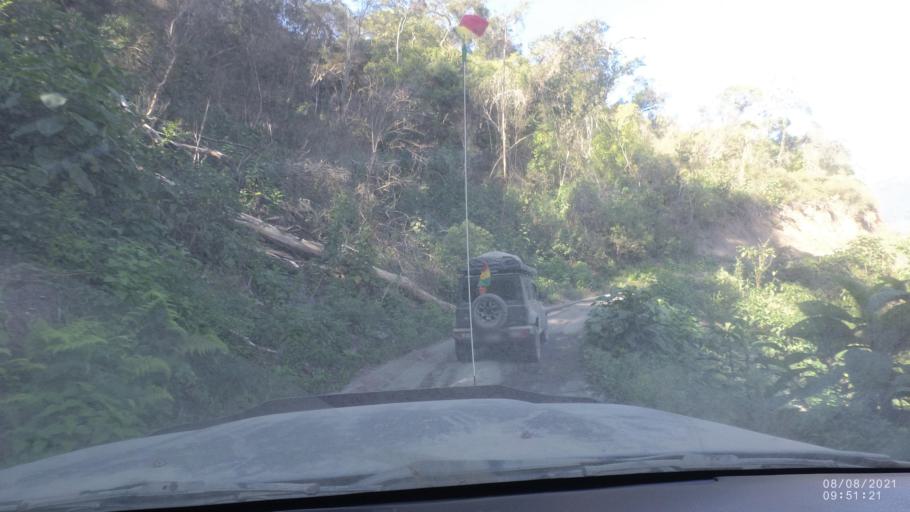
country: BO
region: La Paz
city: Quime
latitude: -16.6228
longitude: -66.7285
